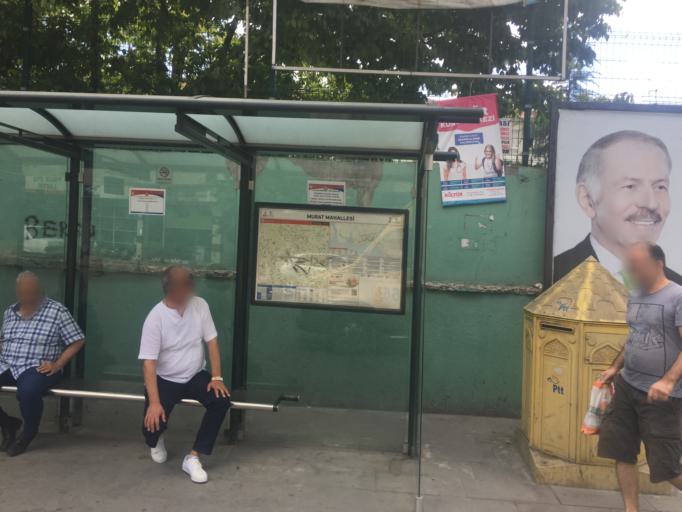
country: TR
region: Istanbul
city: Esenler
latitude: 41.0513
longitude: 28.9058
